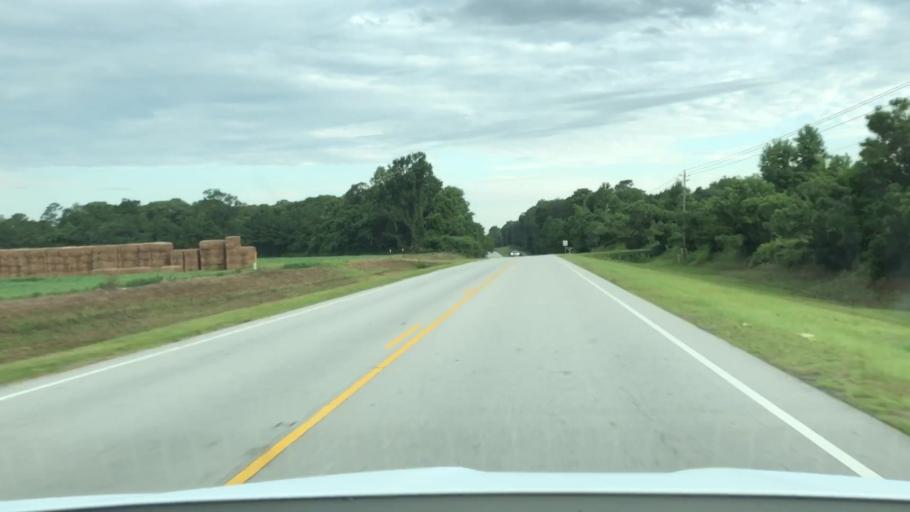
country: US
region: North Carolina
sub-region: Jones County
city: Trenton
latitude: 35.0042
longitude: -77.2781
